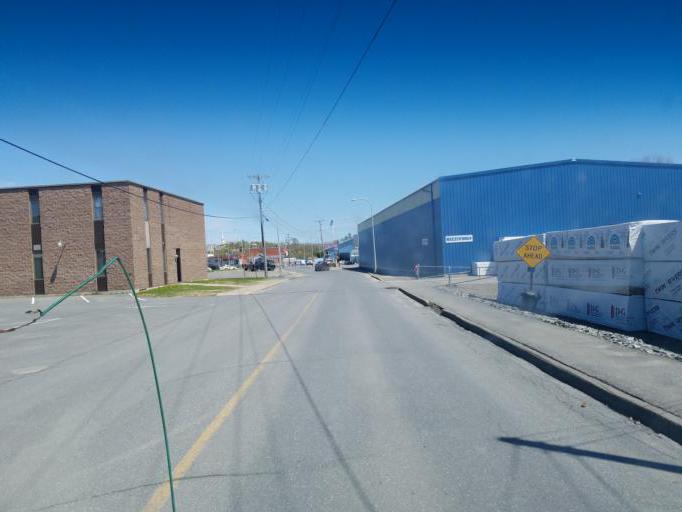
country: US
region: Maine
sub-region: Aroostook County
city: Caribou
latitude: 46.8588
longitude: -68.0166
